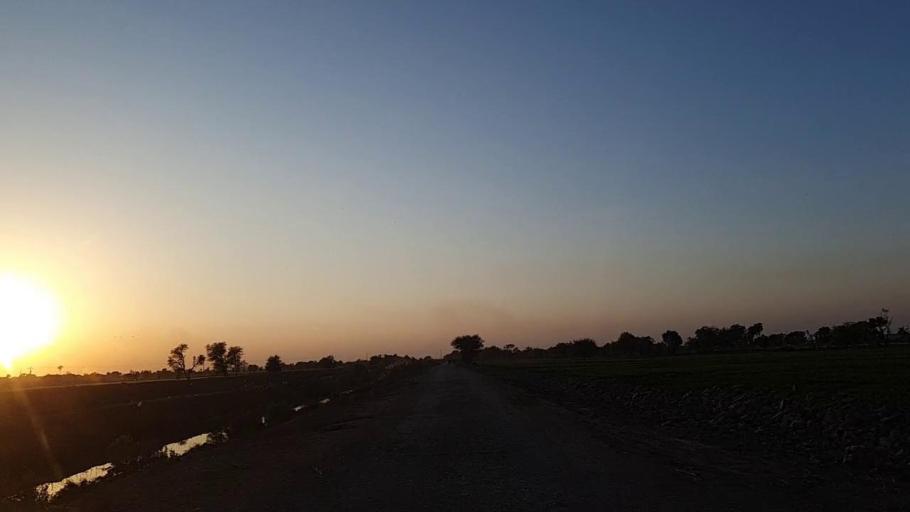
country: PK
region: Sindh
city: Jam Sahib
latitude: 26.3107
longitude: 68.6581
